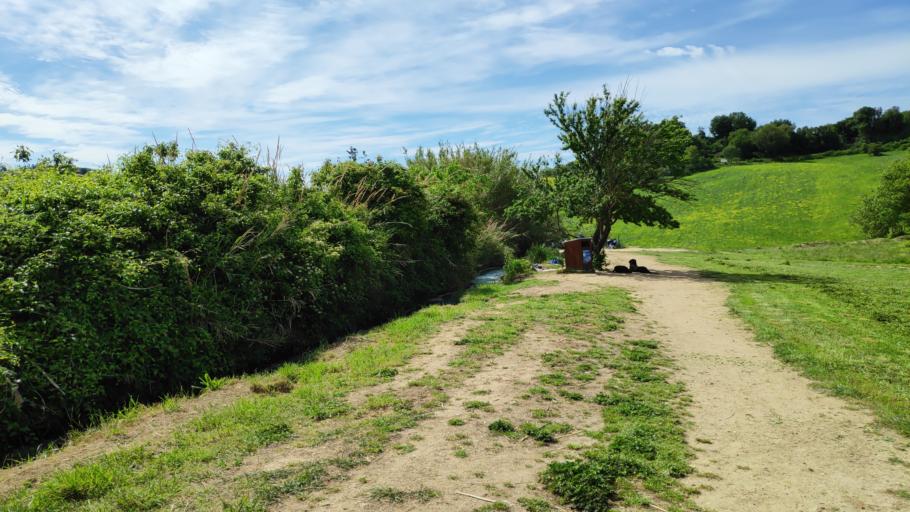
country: IT
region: Tuscany
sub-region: Provincia di Grosseto
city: Manciano
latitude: 42.6490
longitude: 11.5125
